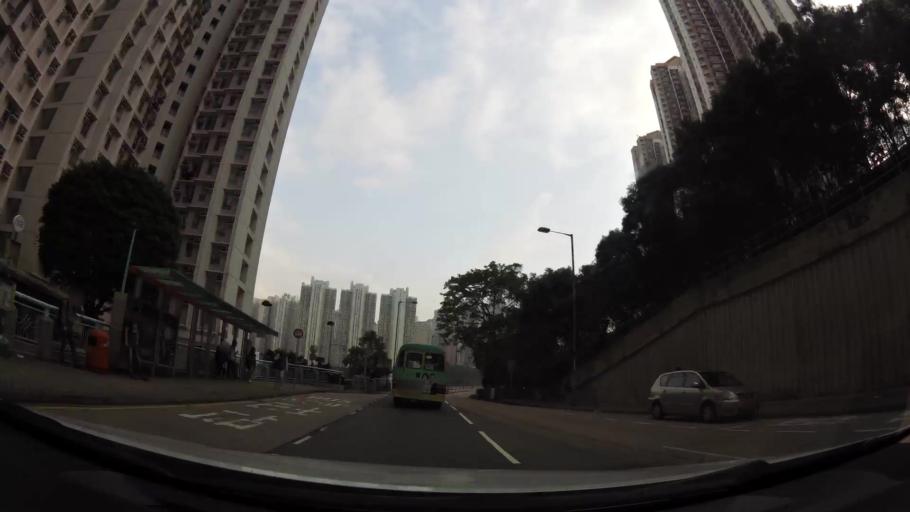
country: HK
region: Kowloon City
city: Kowloon
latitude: 22.3104
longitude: 114.2352
